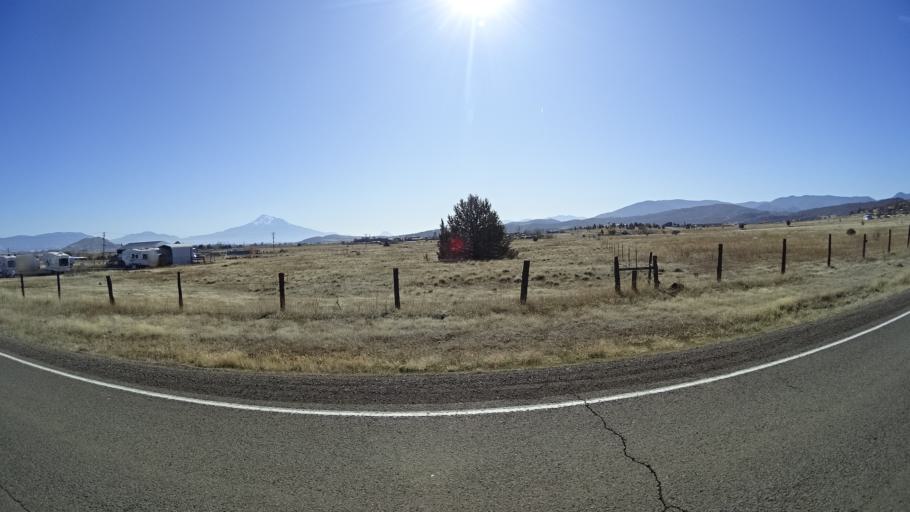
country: US
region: California
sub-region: Siskiyou County
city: Yreka
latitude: 41.7421
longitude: -122.5950
